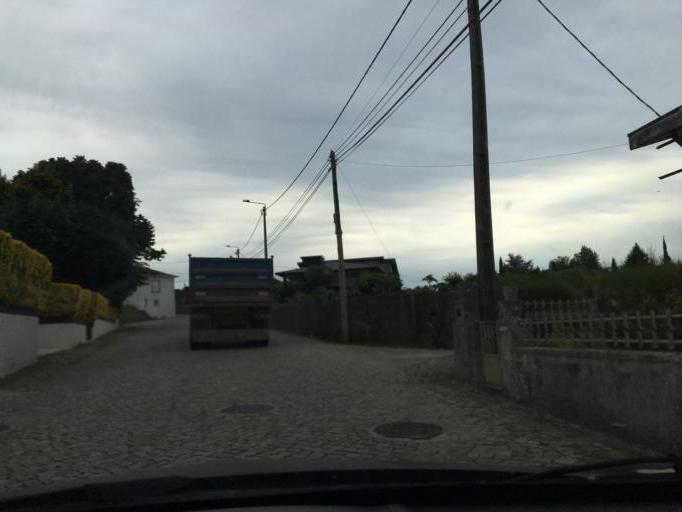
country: PT
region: Porto
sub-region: Maia
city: Anta
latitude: 41.2813
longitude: -8.6142
